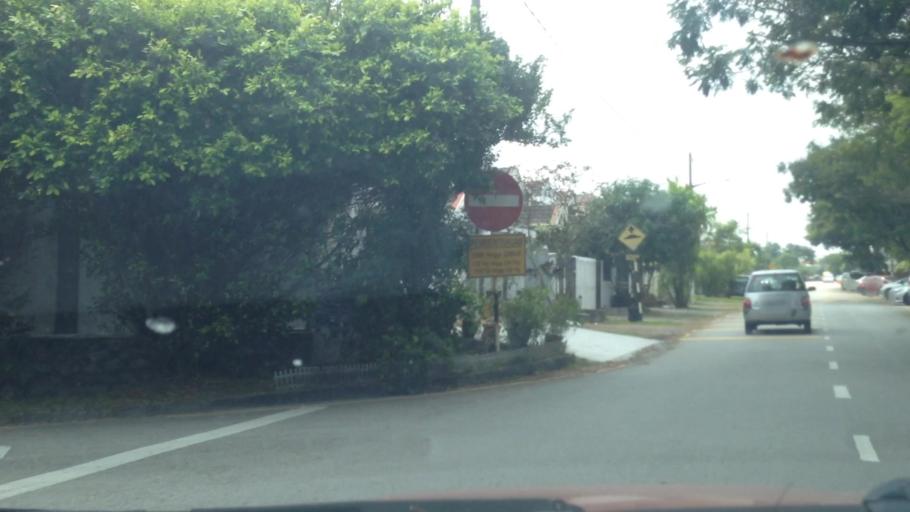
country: MY
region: Selangor
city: Subang Jaya
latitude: 3.0564
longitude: 101.5740
